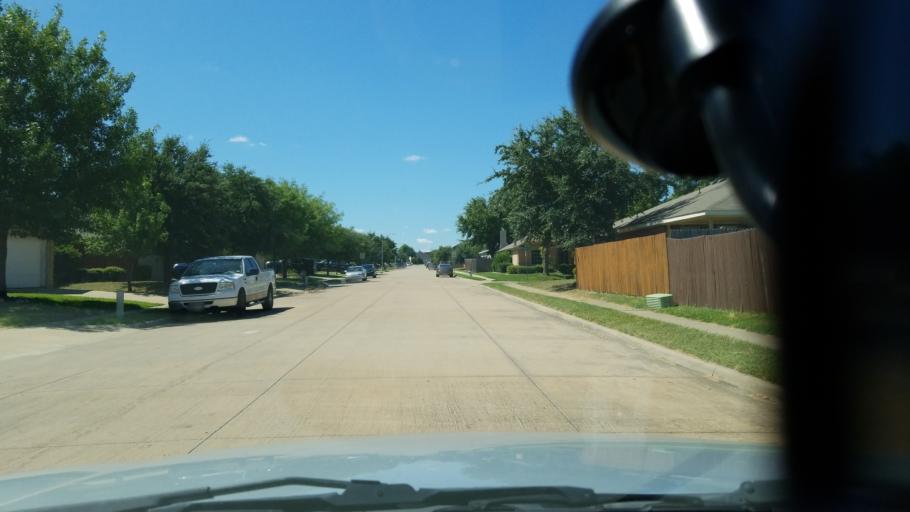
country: US
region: Texas
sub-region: Dallas County
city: Duncanville
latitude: 32.6595
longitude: -96.8649
